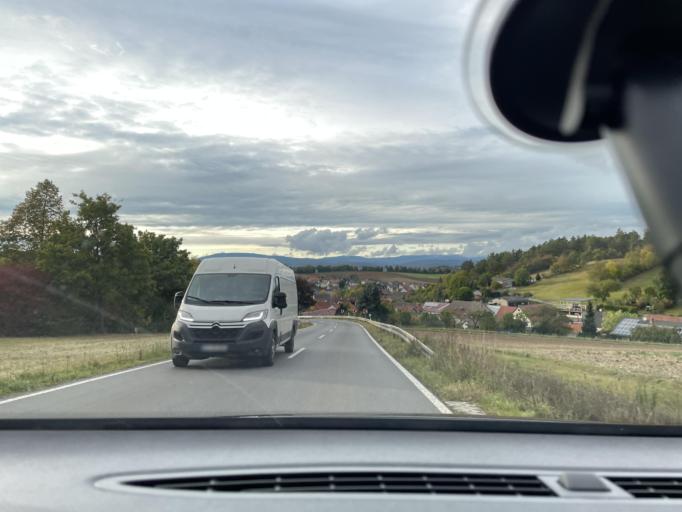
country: DE
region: Bavaria
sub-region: Regierungsbezirk Unterfranken
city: Strahlungen
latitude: 50.2980
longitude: 10.2526
